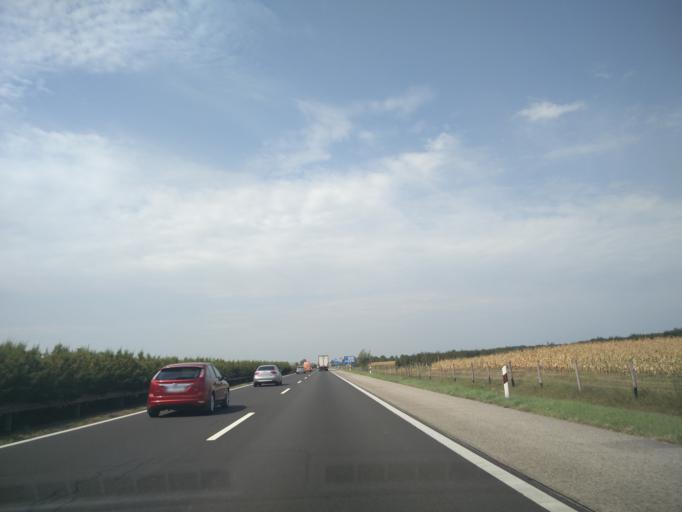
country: HU
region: Bacs-Kiskun
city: Lajosmizse
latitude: 47.0313
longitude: 19.5784
